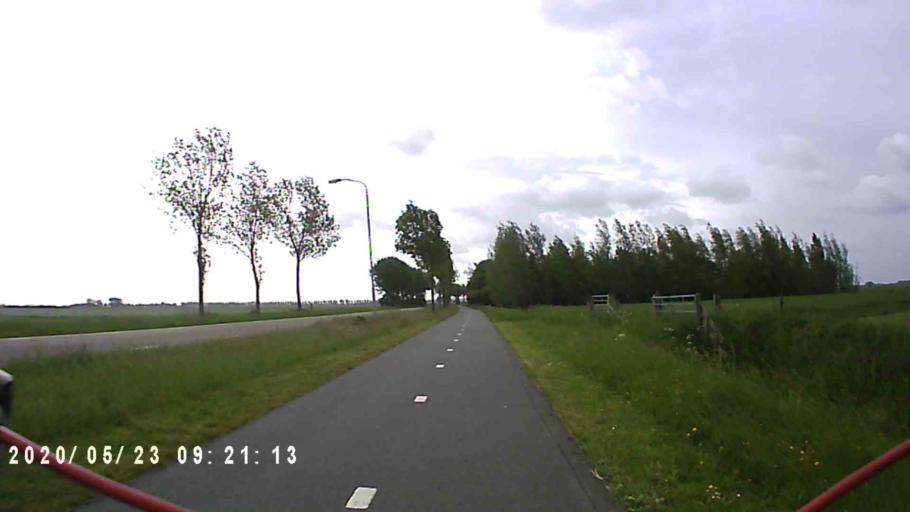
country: NL
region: Groningen
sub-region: Gemeente Bedum
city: Bedum
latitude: 53.2938
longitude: 6.6759
